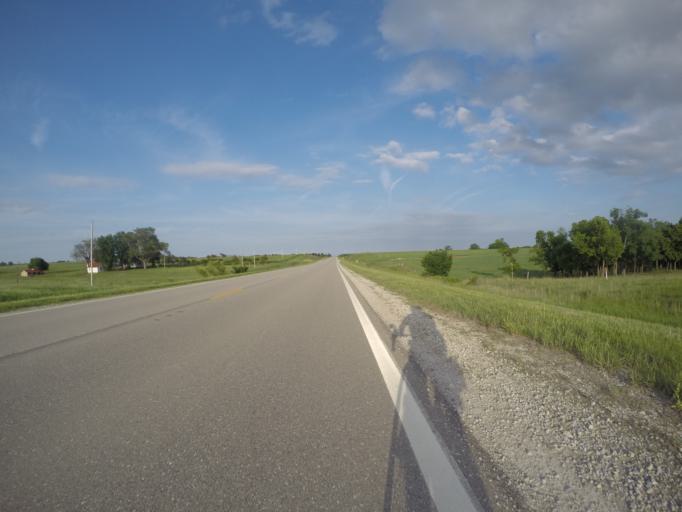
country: US
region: Kansas
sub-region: Pottawatomie County
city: Westmoreland
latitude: 39.4282
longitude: -96.5924
